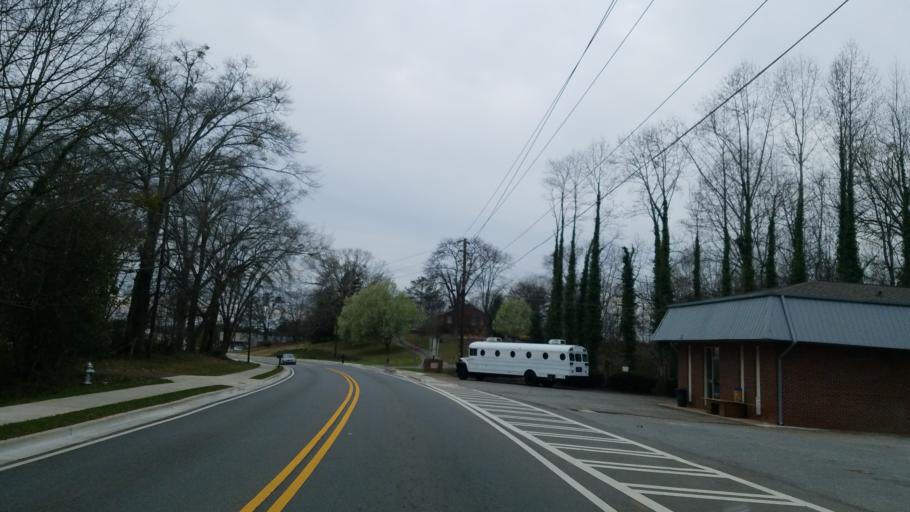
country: US
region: Georgia
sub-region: Cherokee County
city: Canton
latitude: 34.2187
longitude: -84.5019
